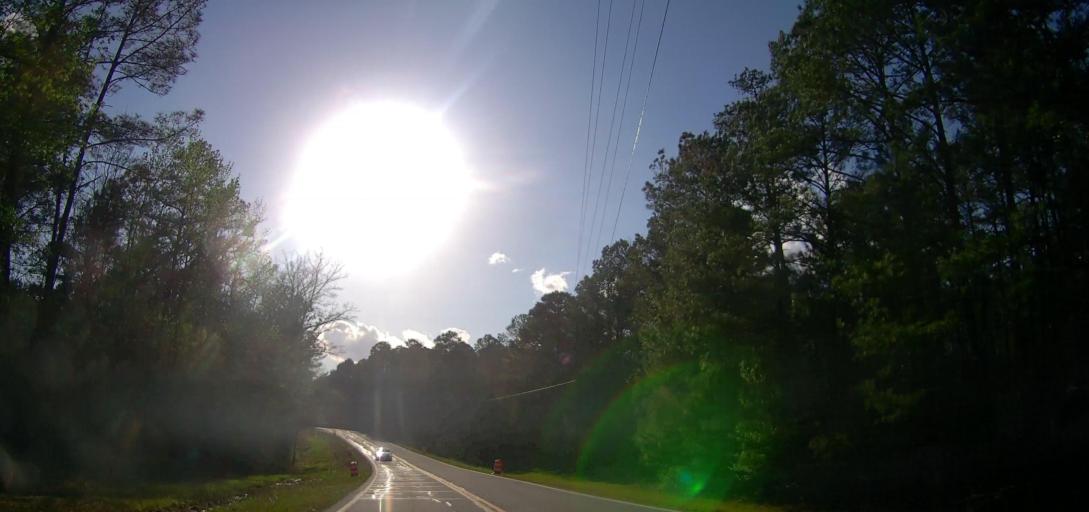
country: US
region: Georgia
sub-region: Baldwin County
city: Milledgeville
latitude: 33.1283
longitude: -83.3071
